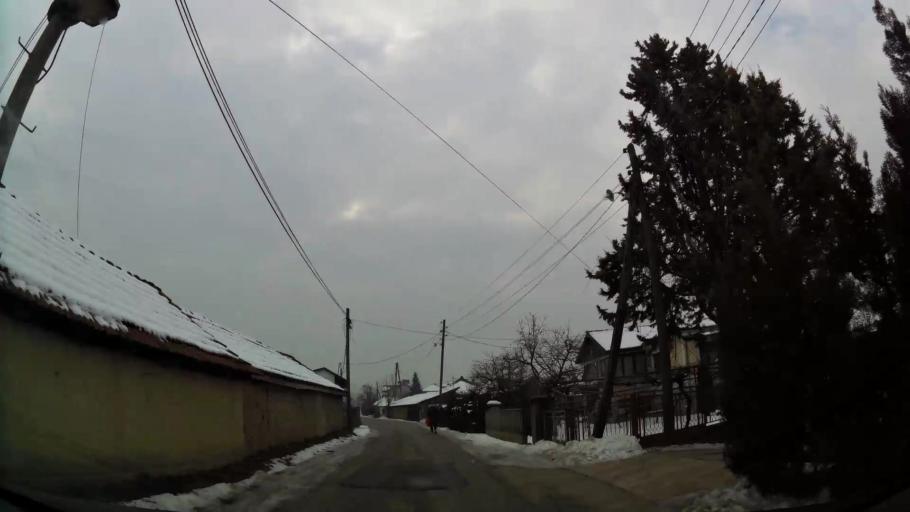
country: MK
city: Kondovo
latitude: 42.0439
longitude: 21.3502
